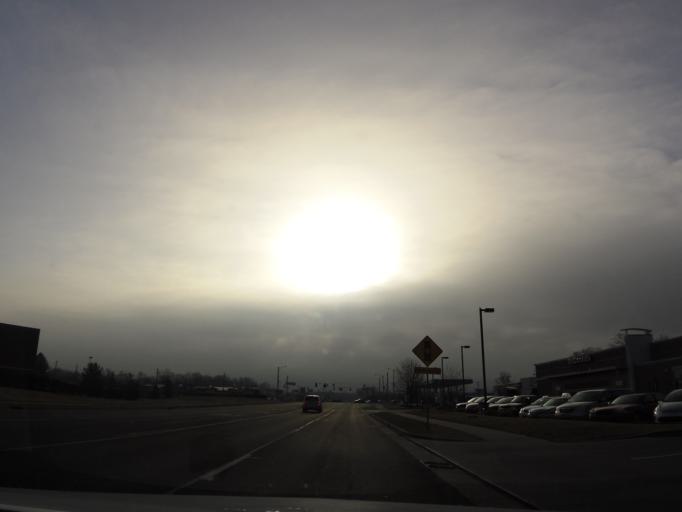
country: US
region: Indiana
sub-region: Bartholomew County
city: Columbus
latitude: 39.2185
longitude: -85.8858
